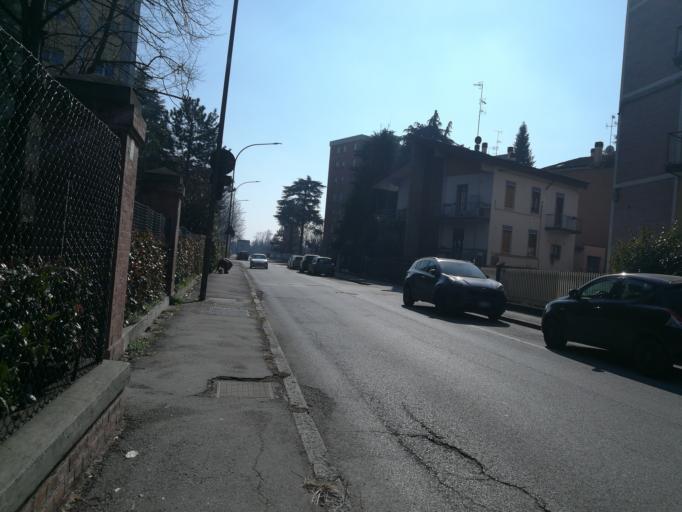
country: IT
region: Emilia-Romagna
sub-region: Provincia di Bologna
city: Progresso
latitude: 44.5436
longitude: 11.3585
